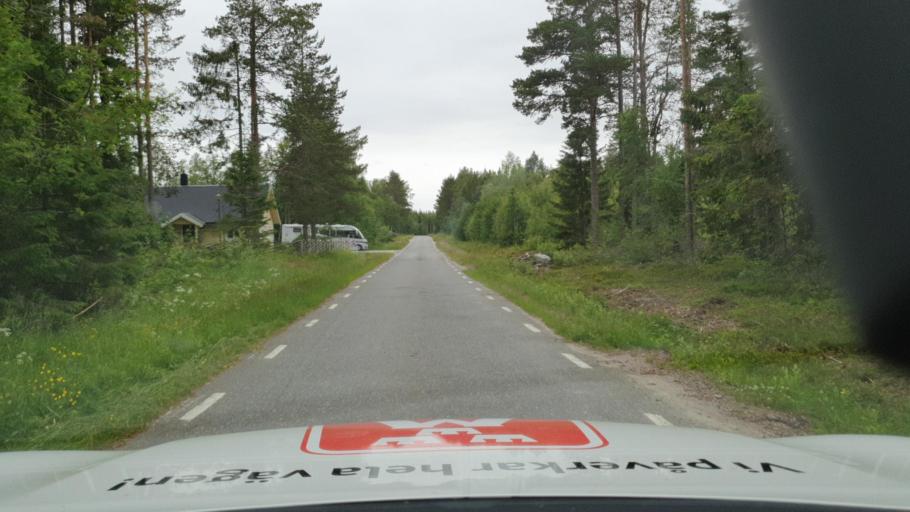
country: SE
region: Vaesterbotten
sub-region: Nordmalings Kommun
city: Nordmaling
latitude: 63.4239
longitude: 19.5004
